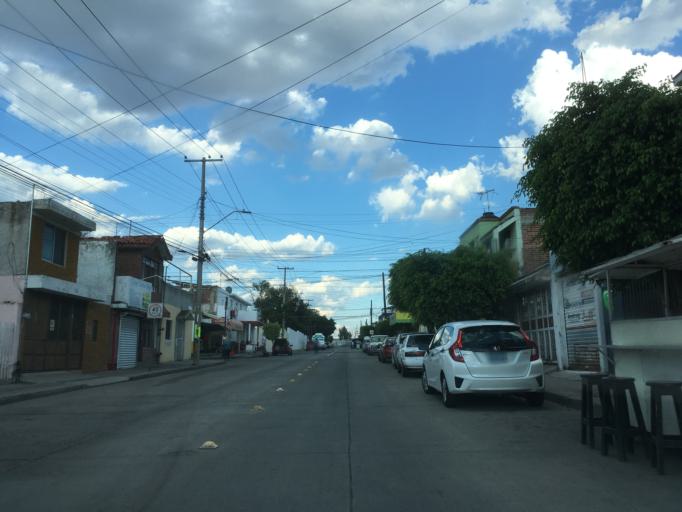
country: MX
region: Guanajuato
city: Leon
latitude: 21.0961
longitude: -101.6403
